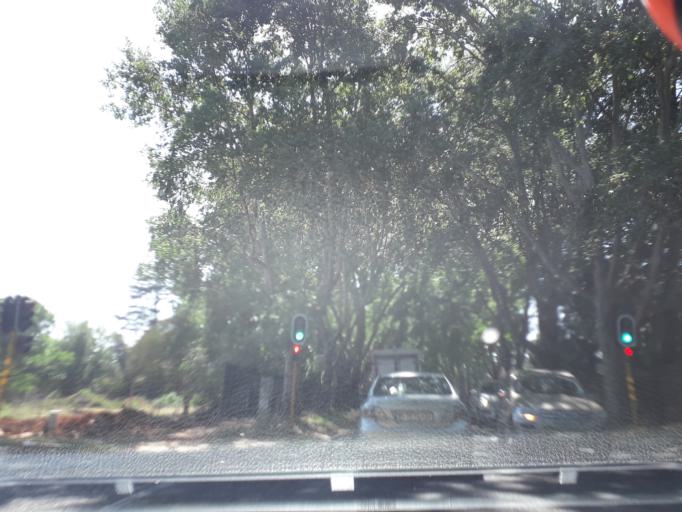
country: ZA
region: Gauteng
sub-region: City of Johannesburg Metropolitan Municipality
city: Johannesburg
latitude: -26.1557
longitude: 28.0535
